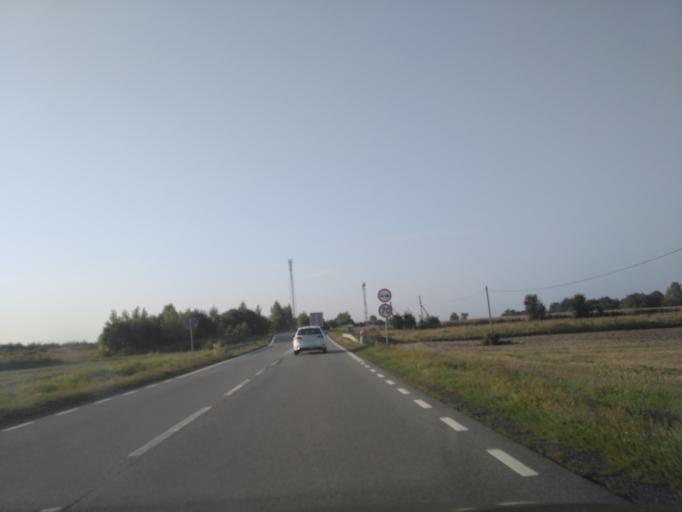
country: PL
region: Lublin Voivodeship
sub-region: Powiat janowski
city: Modliborzyce
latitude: 50.7719
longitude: 22.3252
